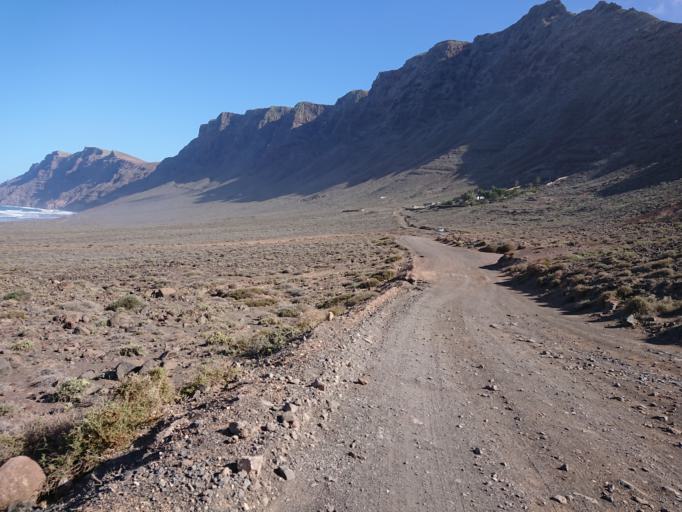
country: ES
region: Canary Islands
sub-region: Provincia de Las Palmas
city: Haria
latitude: 29.1164
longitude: -13.5423
